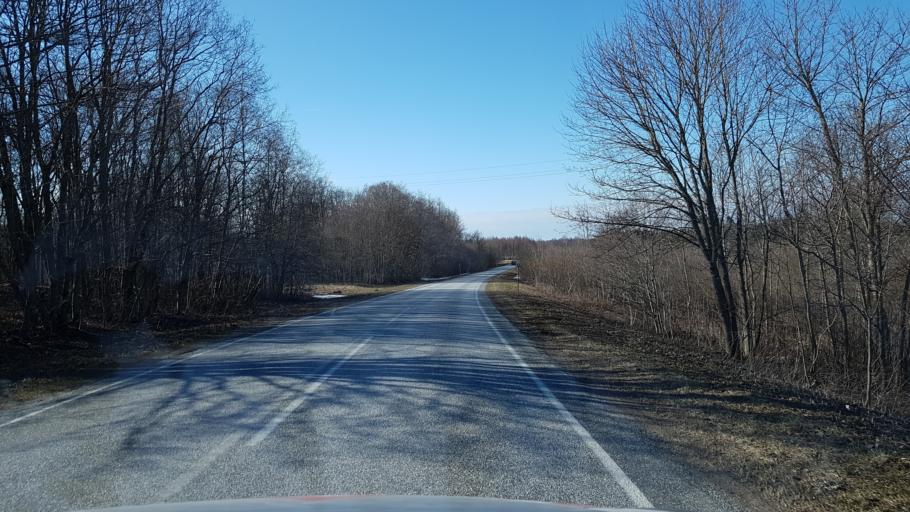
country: EE
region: Laeaene-Virumaa
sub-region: Haljala vald
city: Haljala
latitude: 59.4756
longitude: 26.1620
